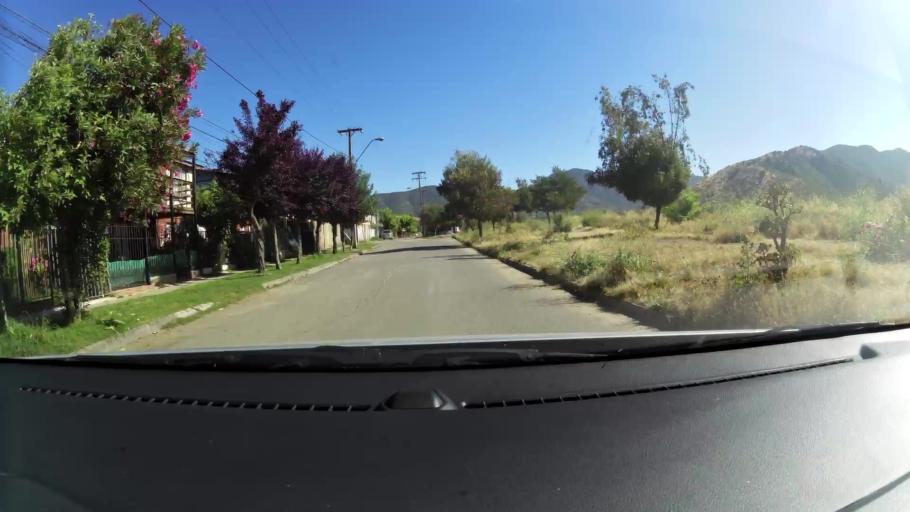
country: CL
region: Santiago Metropolitan
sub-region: Provincia de Chacabuco
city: Lampa
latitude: -33.4064
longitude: -71.1264
